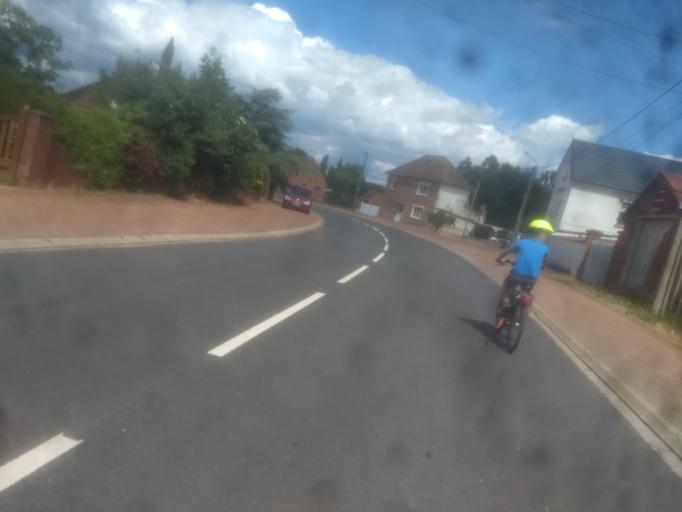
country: FR
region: Nord-Pas-de-Calais
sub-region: Departement du Pas-de-Calais
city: Croisilles
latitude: 50.2223
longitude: 2.8315
